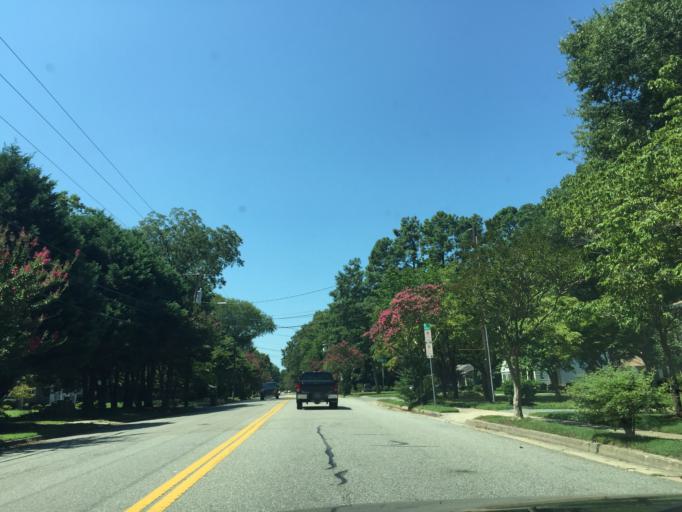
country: US
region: Virginia
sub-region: City of Newport News
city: Newport News
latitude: 37.0600
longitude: -76.4960
